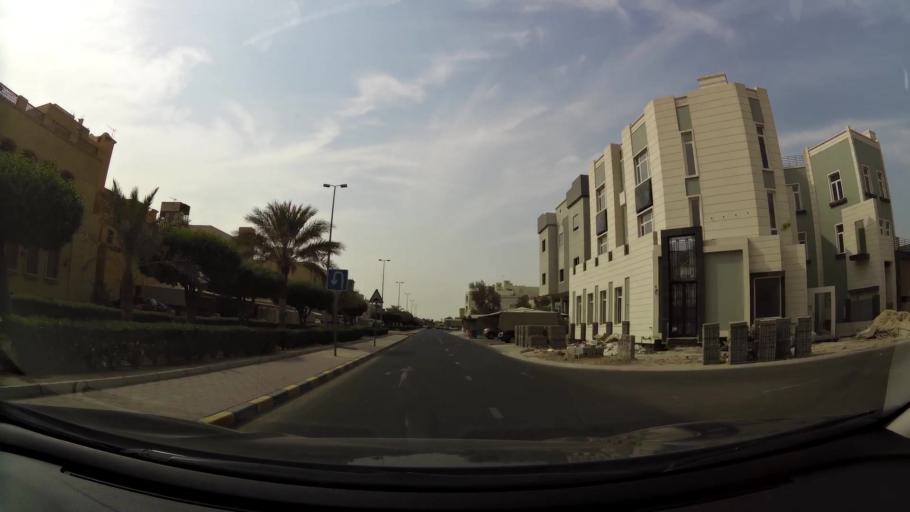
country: KW
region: Al Asimah
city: Ash Shamiyah
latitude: 29.3366
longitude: 47.9650
